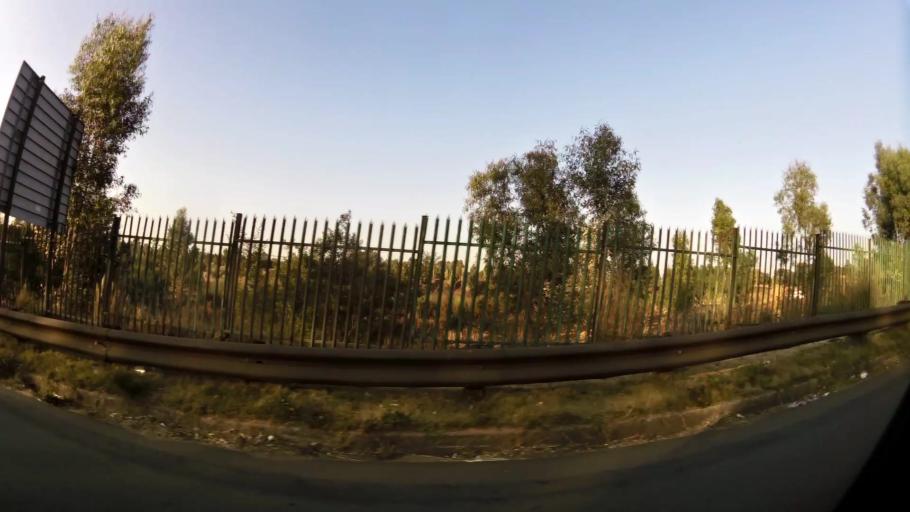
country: ZA
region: Gauteng
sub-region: City of Johannesburg Metropolitan Municipality
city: Johannesburg
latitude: -26.2104
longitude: 27.9911
